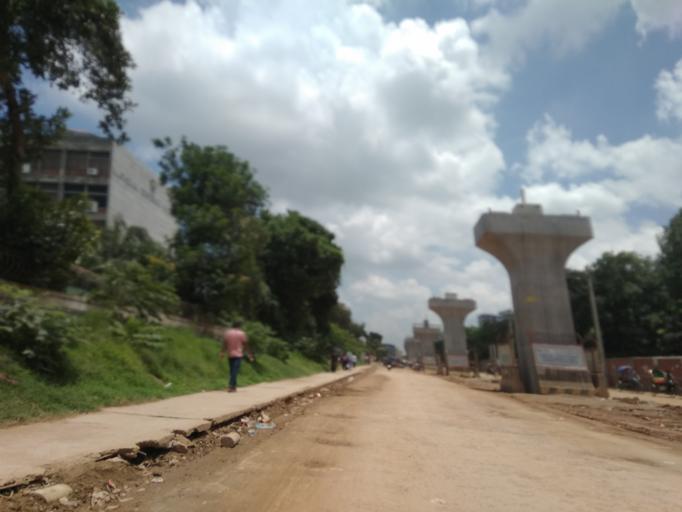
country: BD
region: Dhaka
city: Tungi
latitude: 23.8310
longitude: 90.3637
